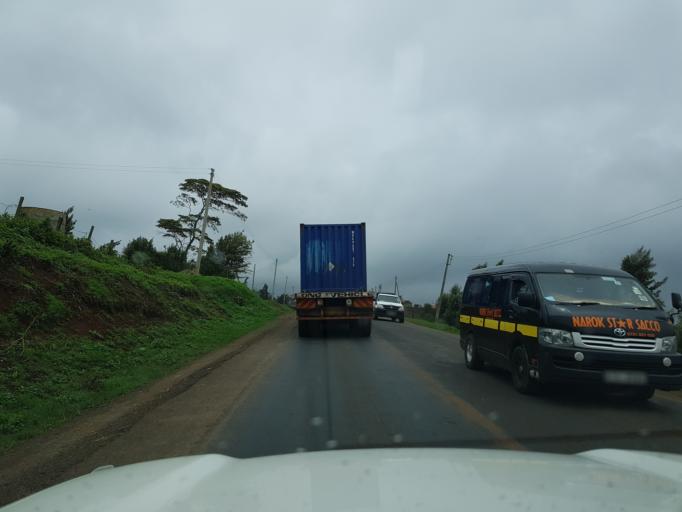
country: KE
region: Kiambu
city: Limuru
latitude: -1.1312
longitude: 36.6304
